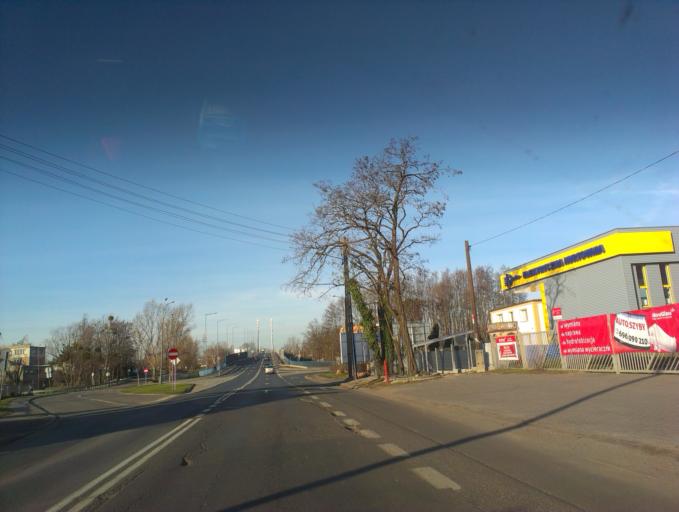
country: PL
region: Greater Poland Voivodeship
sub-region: Powiat poznanski
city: Suchy Las
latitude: 52.4613
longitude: 16.8927
